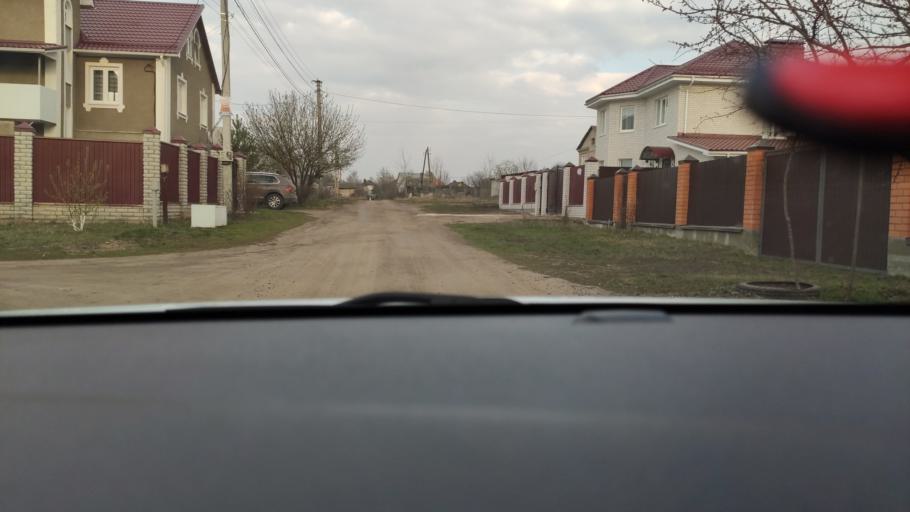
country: RU
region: Voronezj
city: Pridonskoy
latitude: 51.6323
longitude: 39.0872
